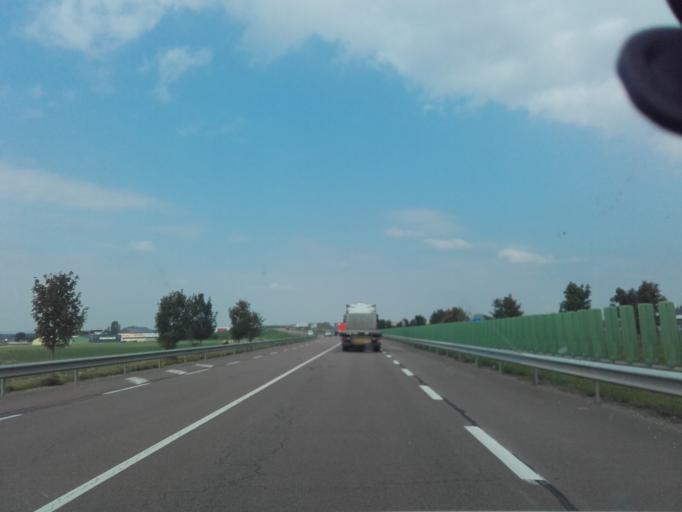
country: FR
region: Bourgogne
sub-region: Departement de Saone-et-Loire
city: Champforgeuil
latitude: 46.8212
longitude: 4.8290
